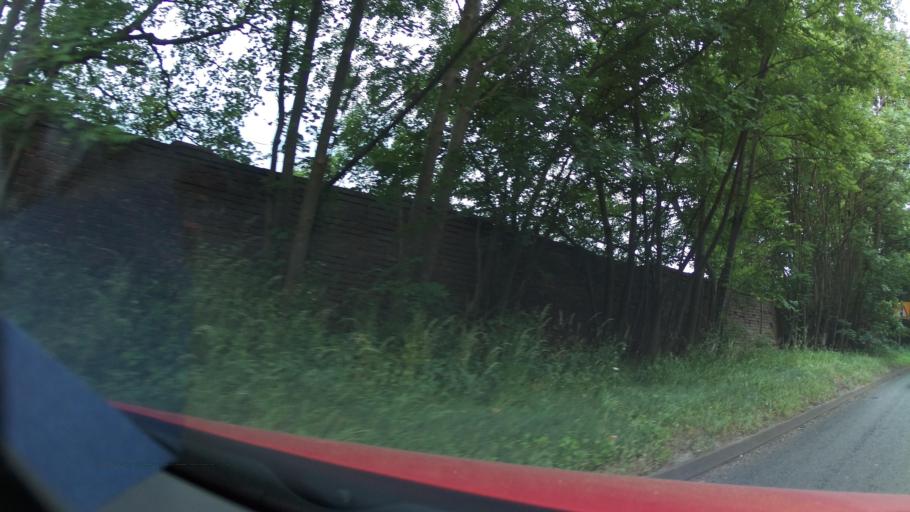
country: GB
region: England
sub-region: Dudley
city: Kingswinford
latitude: 52.5216
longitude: -2.1759
